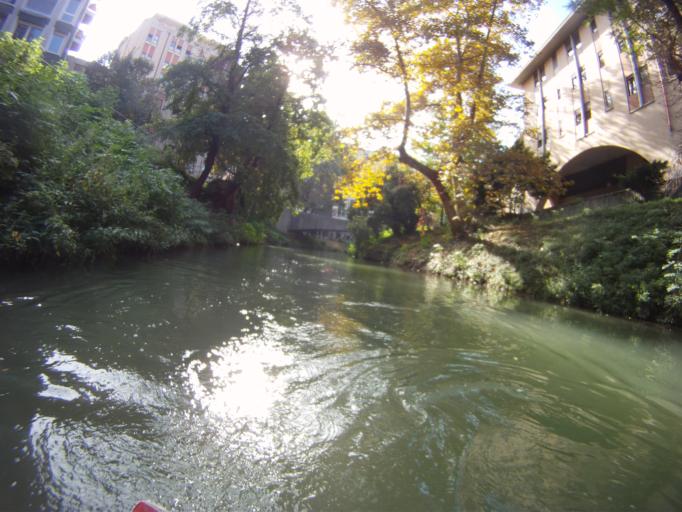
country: IT
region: Veneto
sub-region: Provincia di Padova
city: Padova
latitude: 45.4124
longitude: 11.8753
